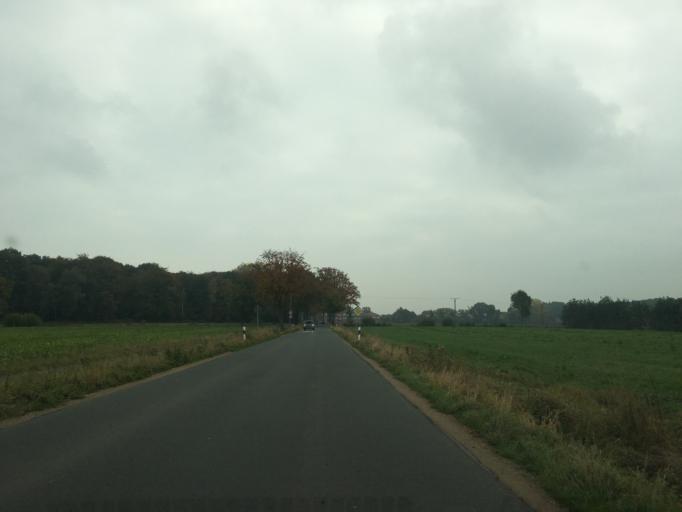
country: DE
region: North Rhine-Westphalia
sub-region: Regierungsbezirk Munster
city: Havixbeck
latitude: 51.9959
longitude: 7.4398
